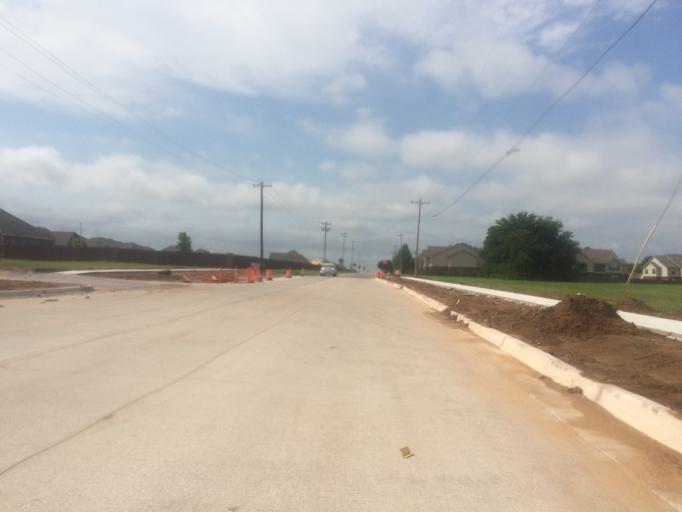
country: US
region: Oklahoma
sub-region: Cleveland County
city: Noble
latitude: 35.1745
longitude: -97.4237
